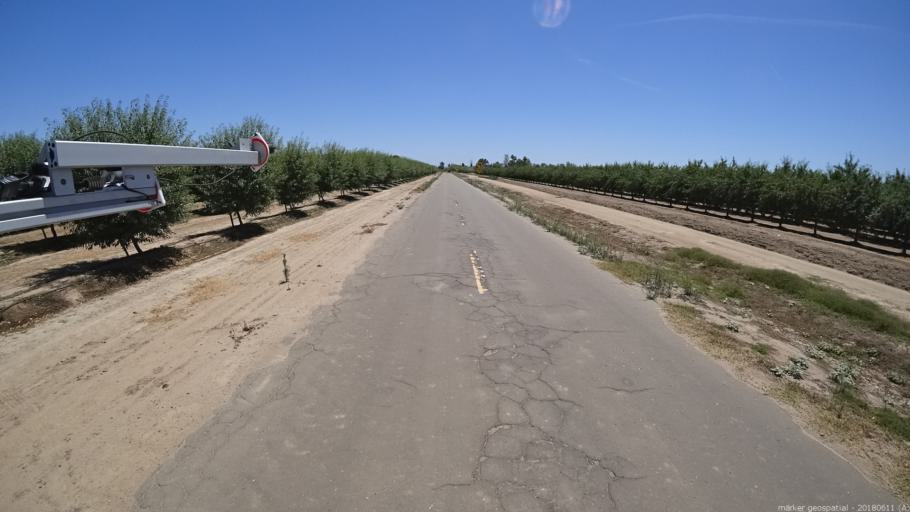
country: US
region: California
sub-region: Madera County
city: Fairmead
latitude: 37.0255
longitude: -120.1883
